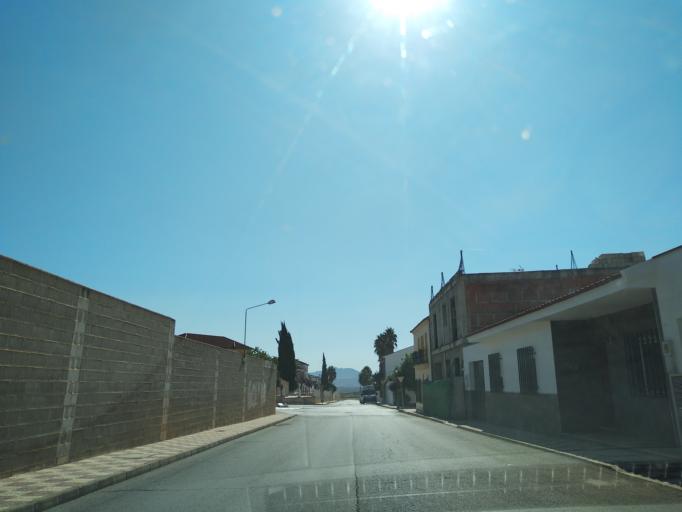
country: ES
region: Andalusia
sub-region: Provincia de Malaga
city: Mollina
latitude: 37.1230
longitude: -4.6556
